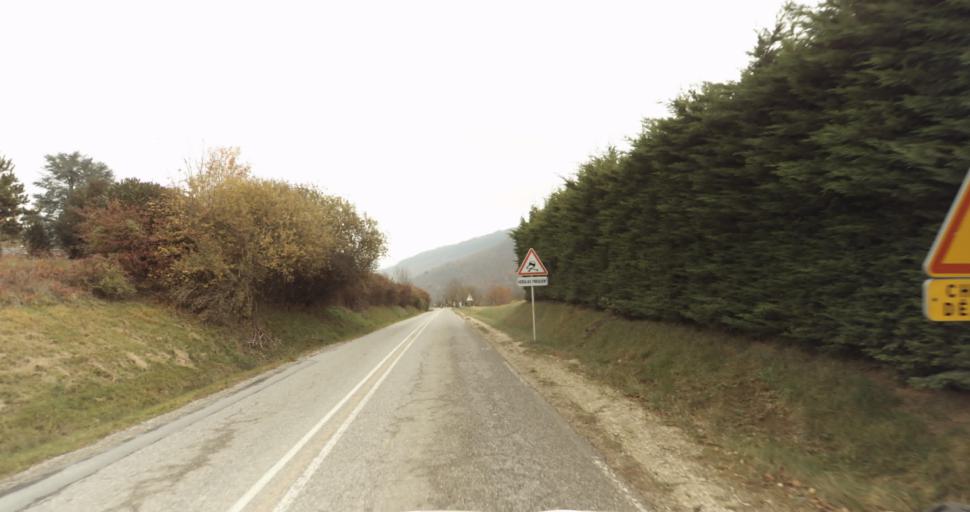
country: FR
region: Rhone-Alpes
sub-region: Departement de la Haute-Savoie
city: Seynod
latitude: 45.8658
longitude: 6.0924
